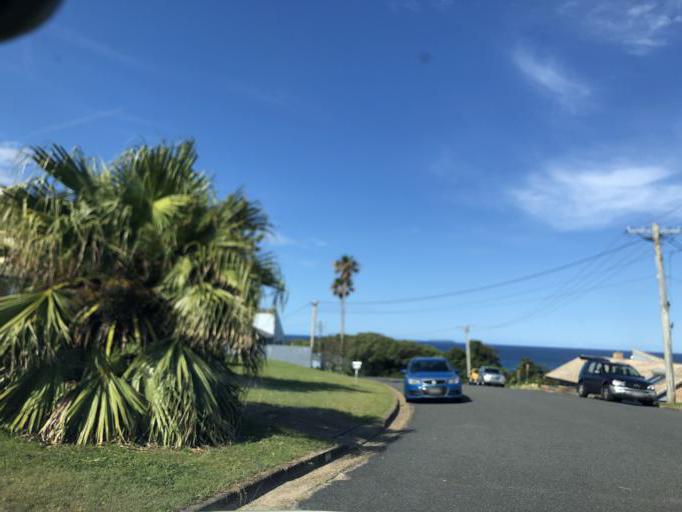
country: AU
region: New South Wales
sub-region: Coffs Harbour
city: Moonee Beach
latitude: -30.2378
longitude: 153.1495
